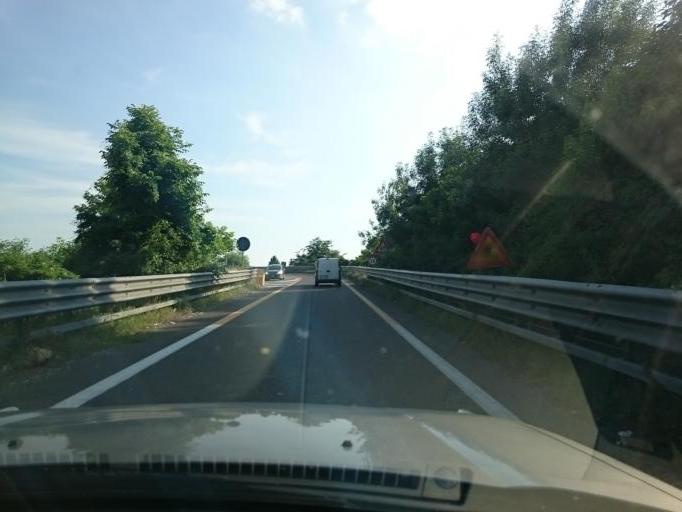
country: IT
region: Veneto
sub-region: Provincia di Padova
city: Mandriola-Sant'Agostino
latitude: 45.3644
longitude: 11.8539
